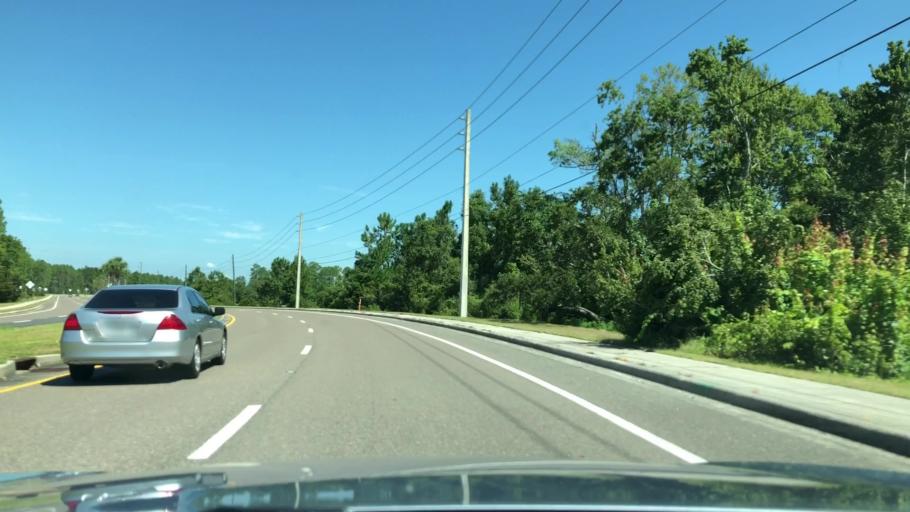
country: US
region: Florida
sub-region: Saint Johns County
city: Fruit Cove
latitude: 30.0870
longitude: -81.5325
